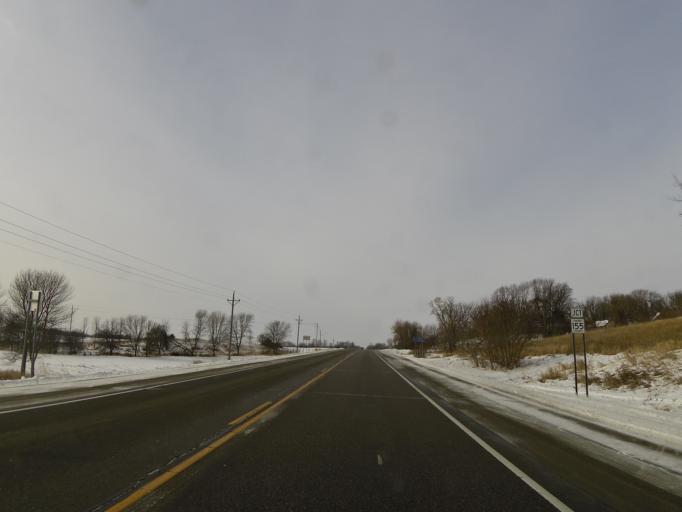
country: US
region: Minnesota
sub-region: Hennepin County
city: Saint Bonifacius
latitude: 44.9053
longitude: -93.7811
